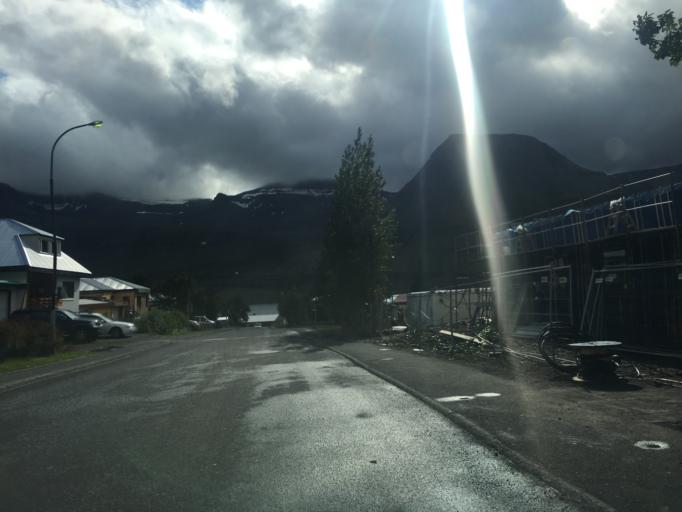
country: IS
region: East
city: Reydarfjoerdur
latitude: 65.0340
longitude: -14.2139
